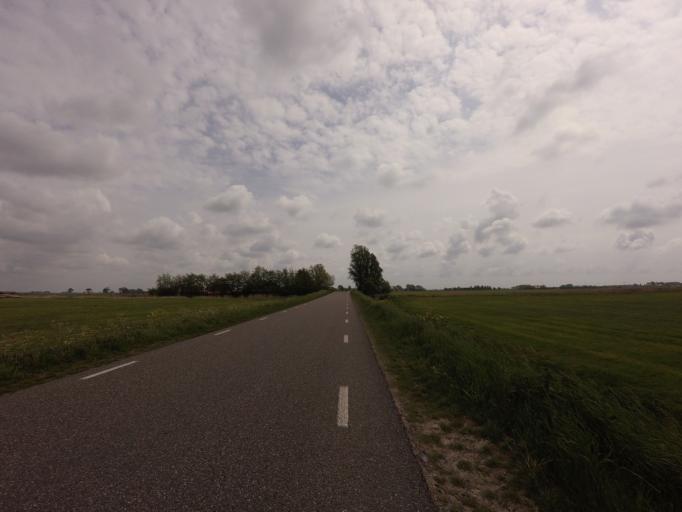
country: NL
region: Friesland
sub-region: Sudwest Fryslan
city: Bolsward
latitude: 53.0967
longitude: 5.5271
